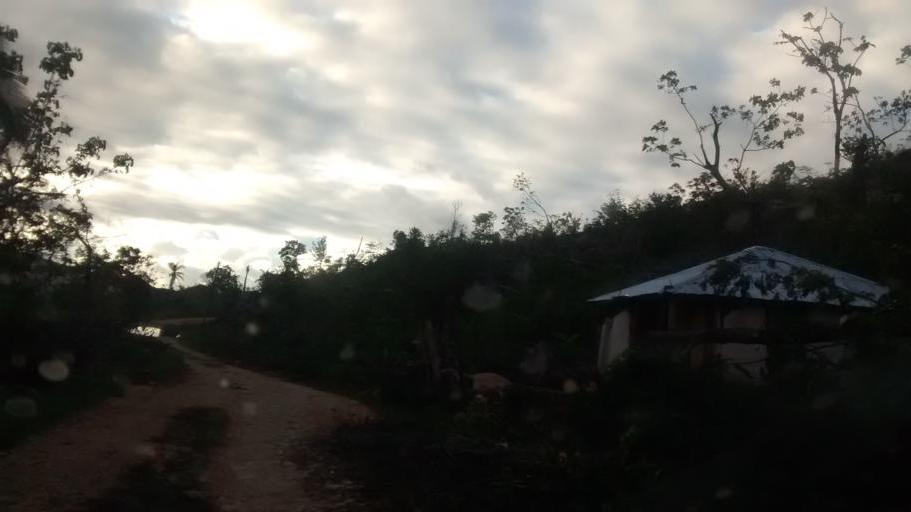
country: HT
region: Grandans
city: Corail
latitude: 18.4774
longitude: -73.7985
